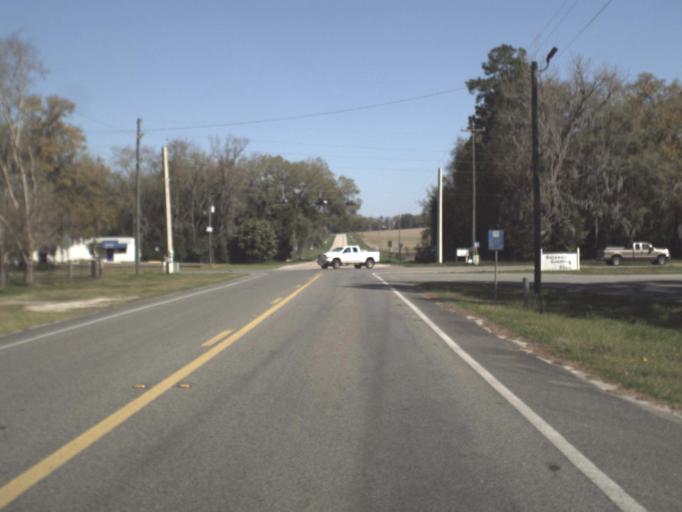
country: US
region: Florida
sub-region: Jefferson County
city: Monticello
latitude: 30.3577
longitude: -83.9901
